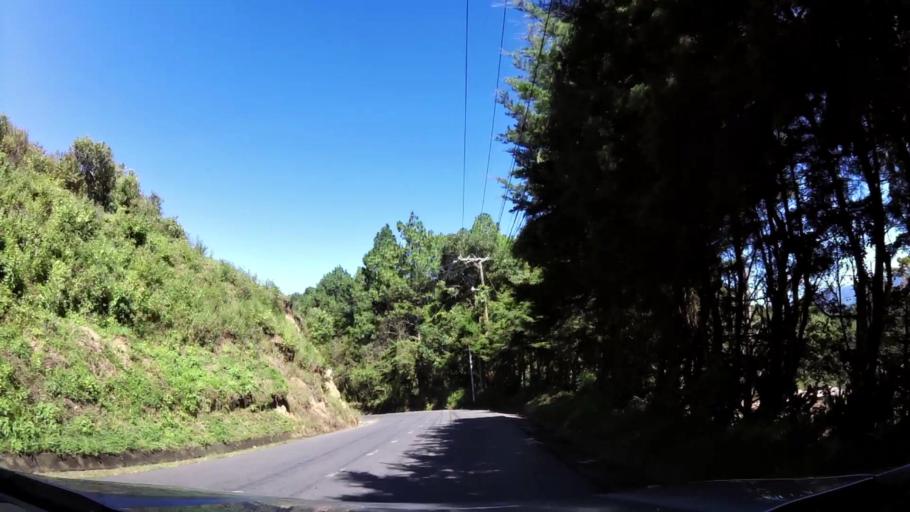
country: GT
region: Guatemala
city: San Jose Pinula
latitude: 14.5143
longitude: -90.4236
